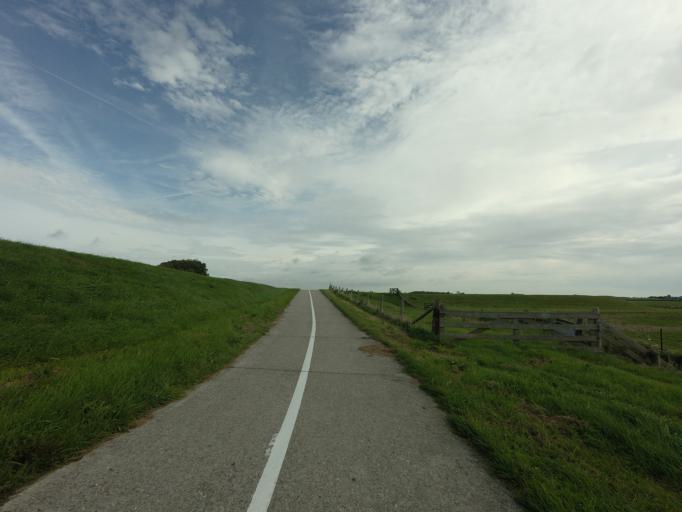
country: NL
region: North Holland
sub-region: Gemeente Texel
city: Den Burg
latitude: 53.0284
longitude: 4.7825
